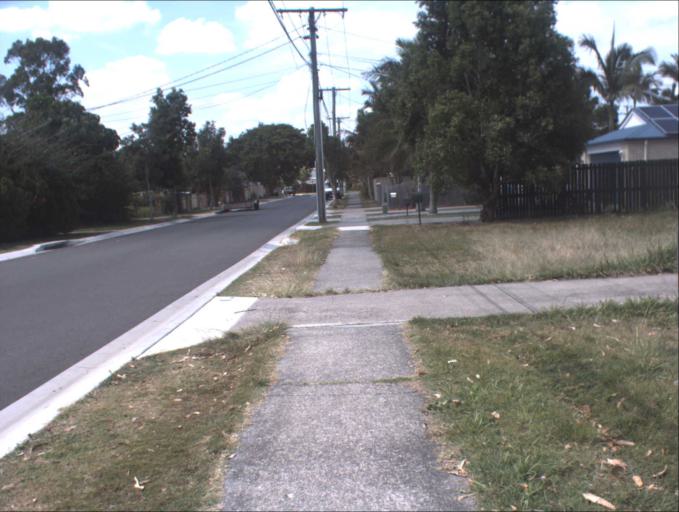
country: AU
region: Queensland
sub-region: Logan
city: Slacks Creek
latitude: -27.6455
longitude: 153.1584
